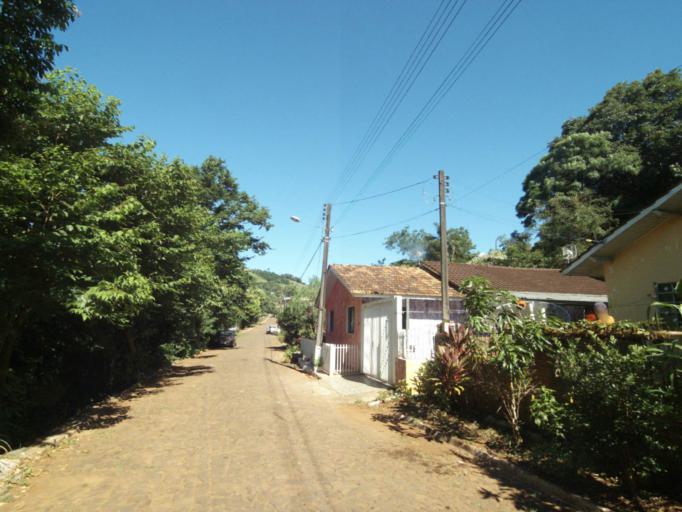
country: BR
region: Parana
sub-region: Ampere
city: Ampere
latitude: -26.1688
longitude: -53.3666
